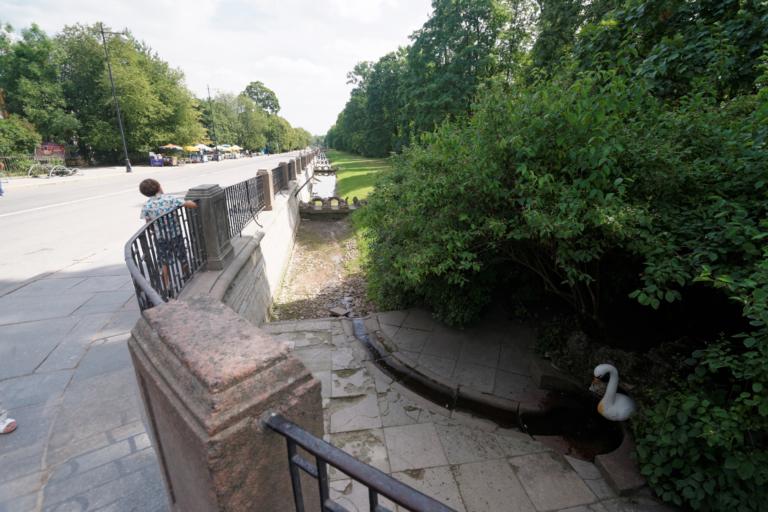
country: RU
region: St.-Petersburg
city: Pushkin
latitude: 59.7170
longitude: 30.3976
